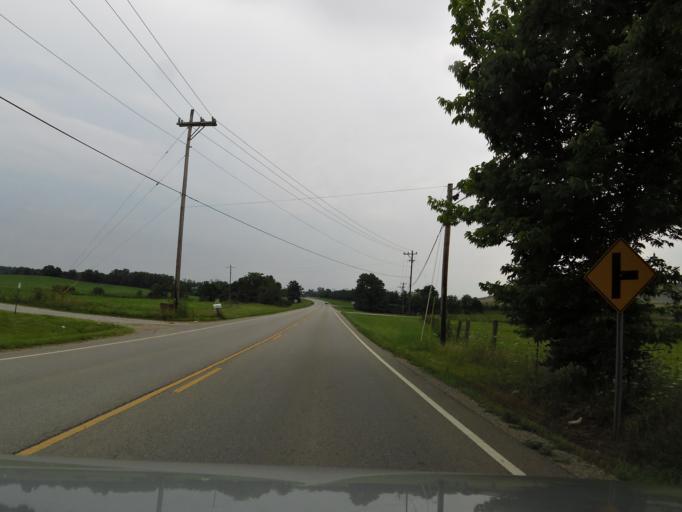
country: US
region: Ohio
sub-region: Brown County
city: Georgetown
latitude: 38.9041
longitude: -83.9024
